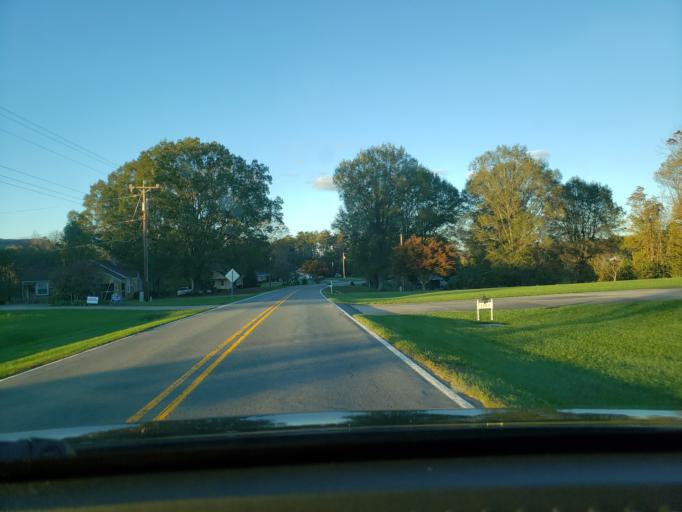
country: US
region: North Carolina
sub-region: Stokes County
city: Danbury
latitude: 36.3538
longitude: -80.2158
